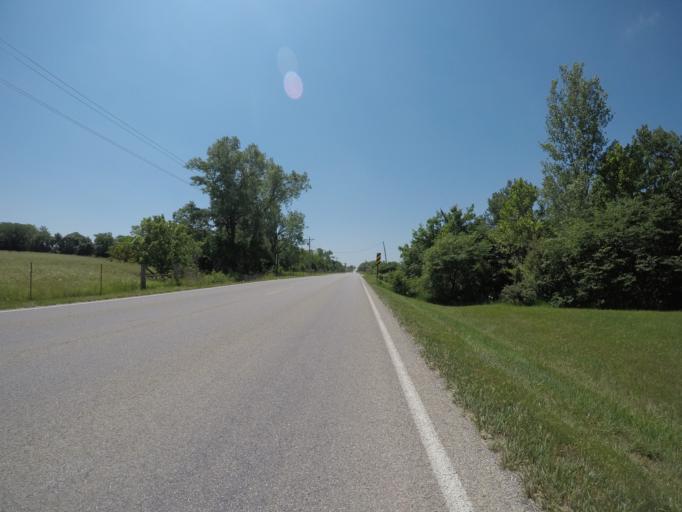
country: US
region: Kansas
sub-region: Pottawatomie County
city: Westmoreland
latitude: 39.2697
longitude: -96.4451
